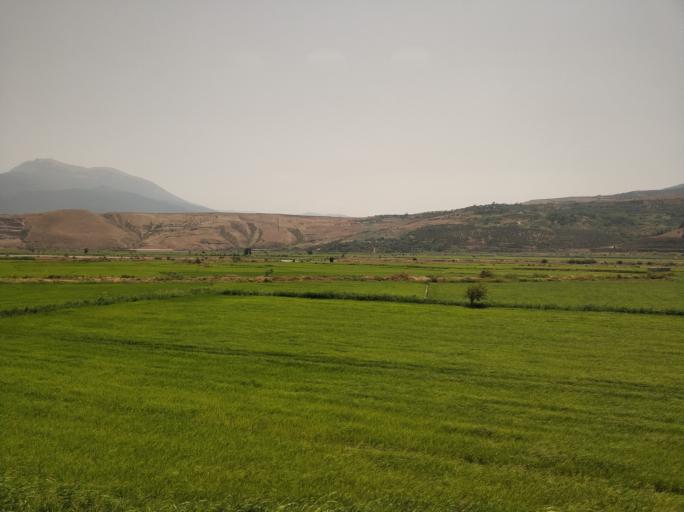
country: IR
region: Gilan
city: Pa'in-e Bazar-e Rudbar
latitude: 36.8801
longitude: 49.4971
